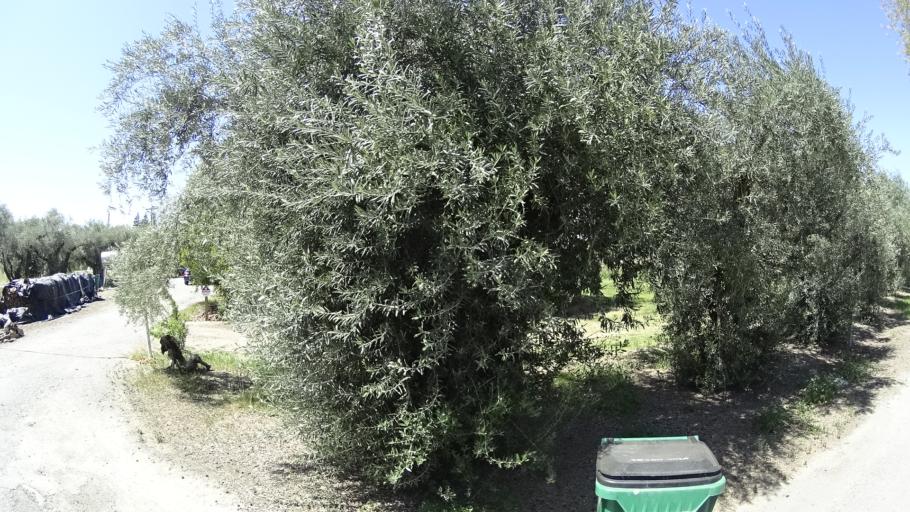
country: US
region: California
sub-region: Glenn County
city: Orland
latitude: 39.7367
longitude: -122.1898
